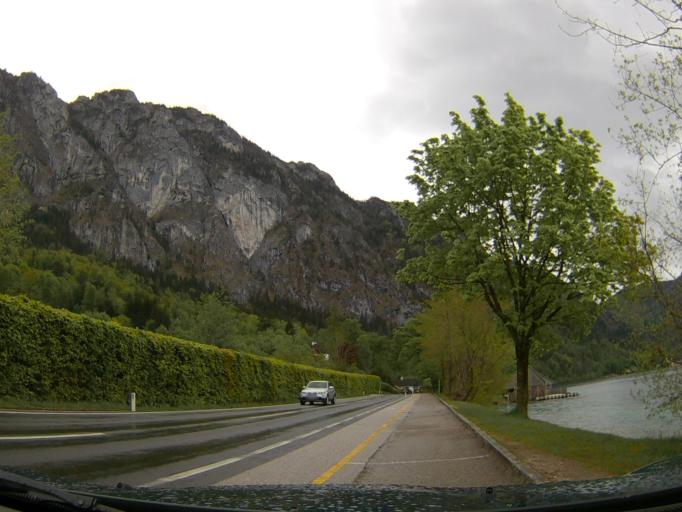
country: AT
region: Upper Austria
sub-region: Politischer Bezirk Vocklabruck
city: Steinbach am Attersee
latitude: 47.8133
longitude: 13.5466
